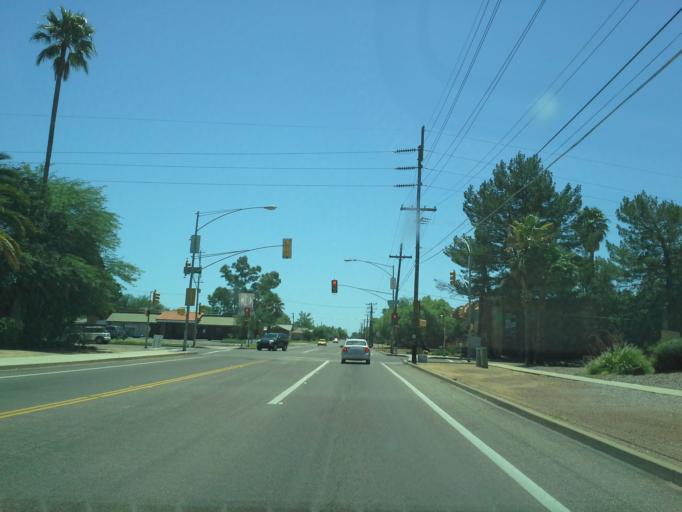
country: US
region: Arizona
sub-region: Pima County
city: Tucson
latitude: 32.2581
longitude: -110.9353
